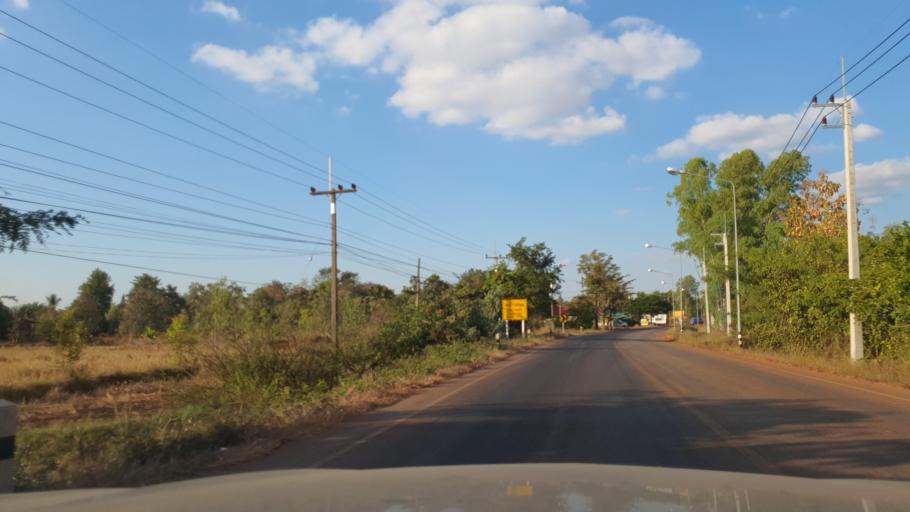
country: TH
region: Sakon Nakhon
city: Phon Na Kaeo
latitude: 17.2690
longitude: 104.1915
